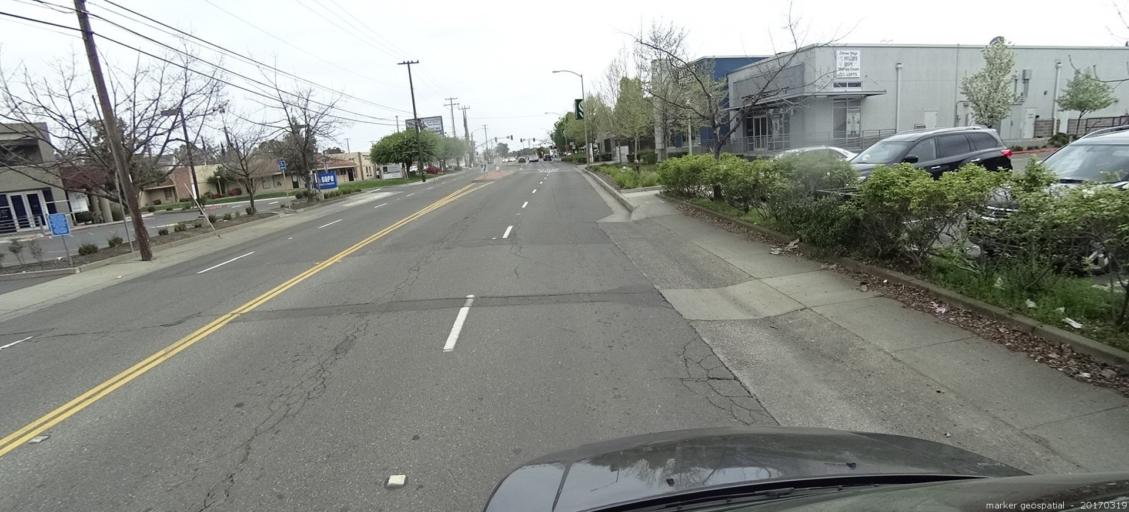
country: US
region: California
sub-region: Sacramento County
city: Florin
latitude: 38.5551
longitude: -121.4296
